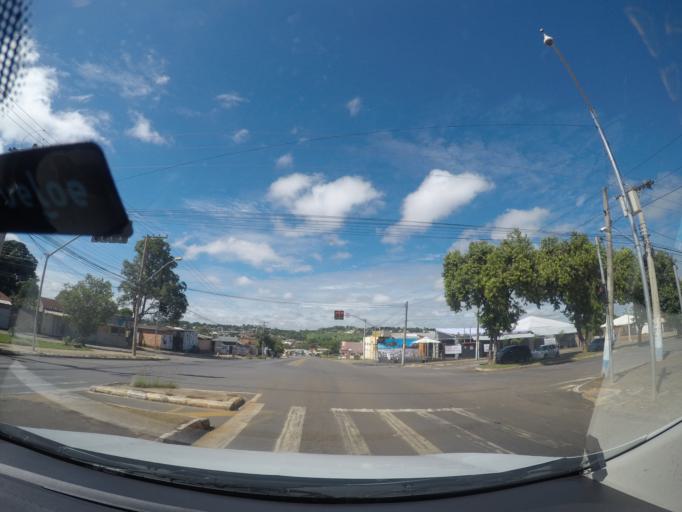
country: BR
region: Goias
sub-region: Goiania
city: Goiania
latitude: -16.6286
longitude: -49.2850
